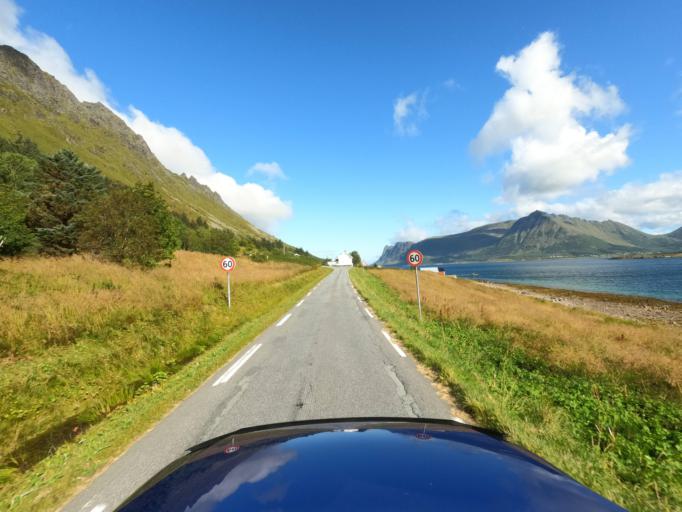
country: NO
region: Nordland
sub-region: Vagan
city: Kabelvag
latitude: 68.2684
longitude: 14.2489
